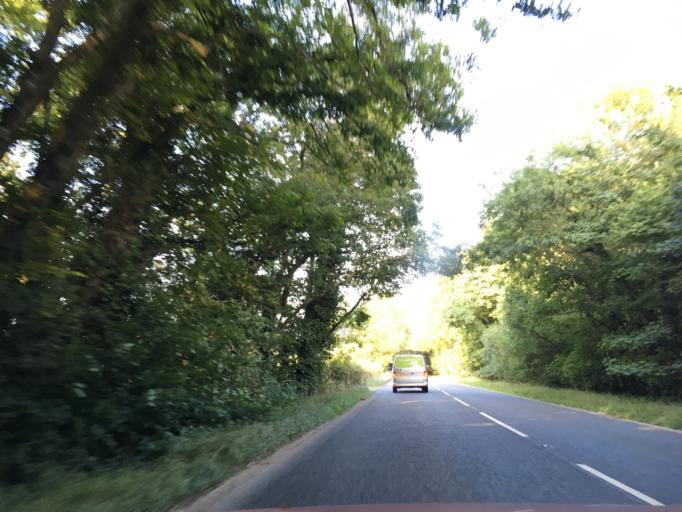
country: GB
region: England
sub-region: Gloucestershire
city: Stow on the Wold
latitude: 51.9037
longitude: -1.7442
